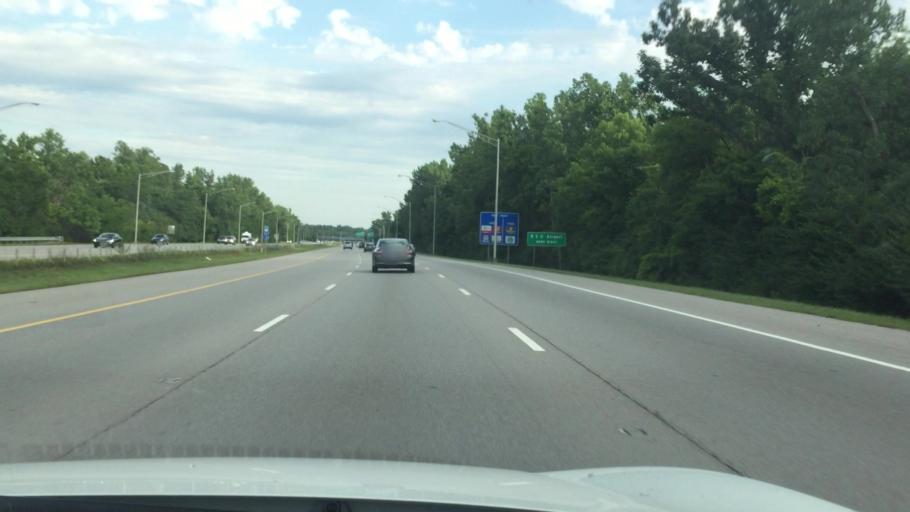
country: US
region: Ohio
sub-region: Franklin County
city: Worthington
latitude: 40.0724
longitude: -83.0355
